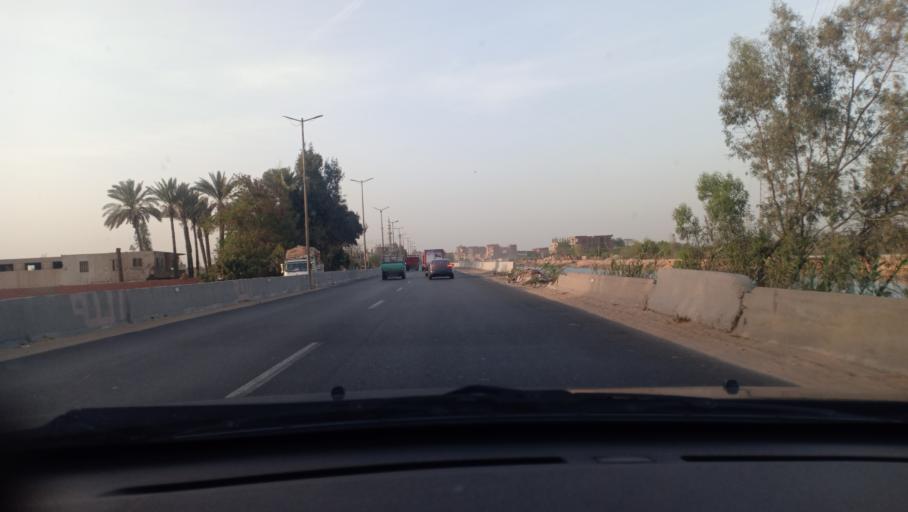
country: EG
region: Muhafazat al Minufiyah
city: Quwaysina
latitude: 30.5677
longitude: 31.2713
